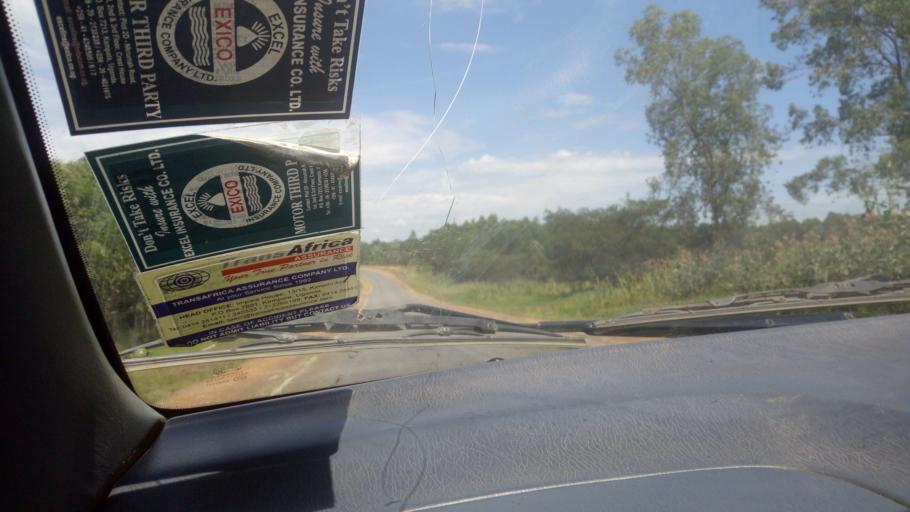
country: UG
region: Western Region
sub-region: Buhweju District
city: Buhweju
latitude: -0.2702
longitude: 30.5623
